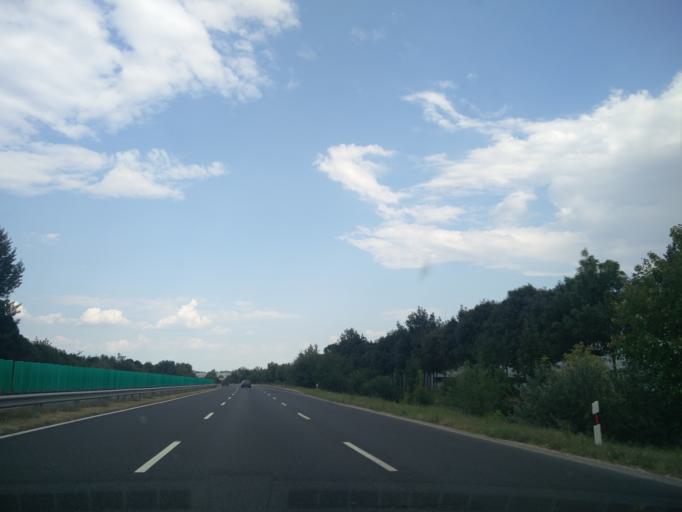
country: HU
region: Fejer
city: Szekesfehervar
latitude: 47.1474
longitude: 18.4159
